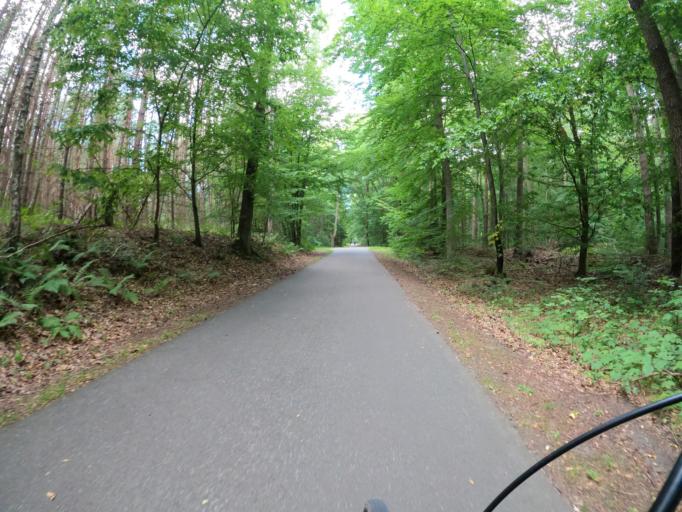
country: DE
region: Brandenburg
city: Angermunde
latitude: 53.0477
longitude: 13.9424
